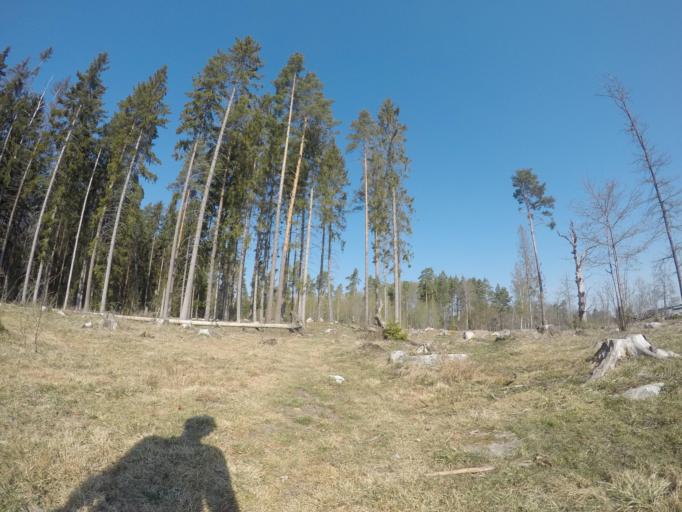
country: SE
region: Vaestmanland
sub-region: Hallstahammars Kommun
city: Kolback
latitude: 59.5305
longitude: 16.2824
